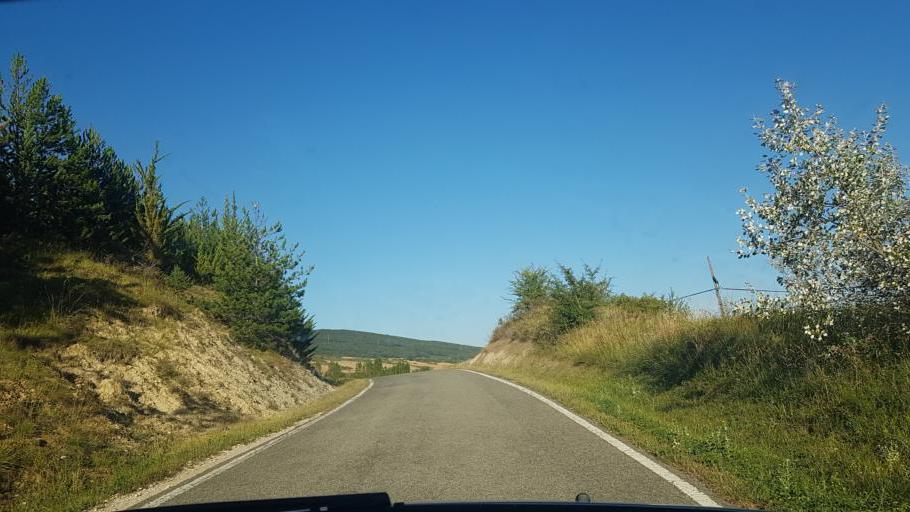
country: ES
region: Navarre
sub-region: Provincia de Navarra
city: Elorz
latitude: 42.7588
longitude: -1.5378
